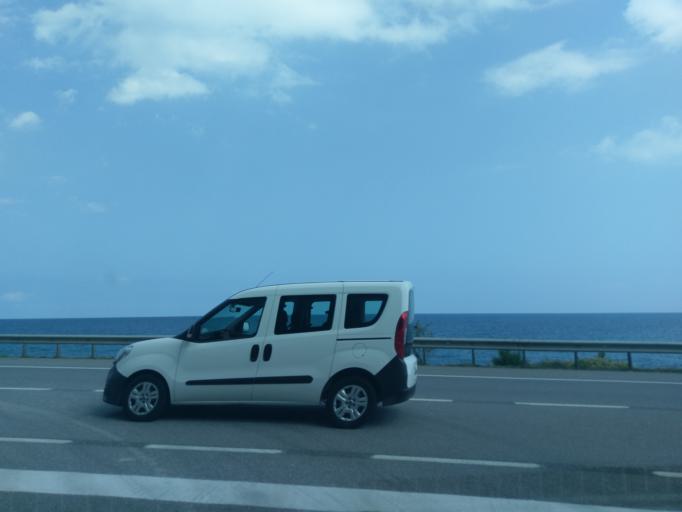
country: TR
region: Sinop
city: Gerze
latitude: 41.7486
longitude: 35.2417
